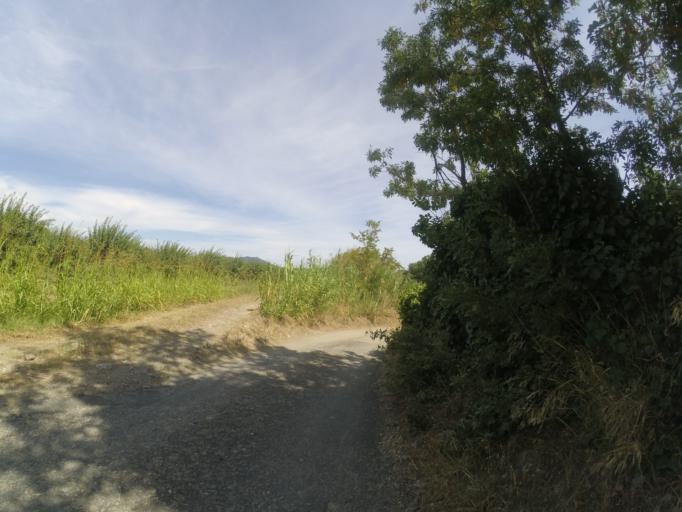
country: FR
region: Languedoc-Roussillon
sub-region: Departement des Pyrenees-Orientales
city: Ille-sur-Tet
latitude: 42.6772
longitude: 2.6484
